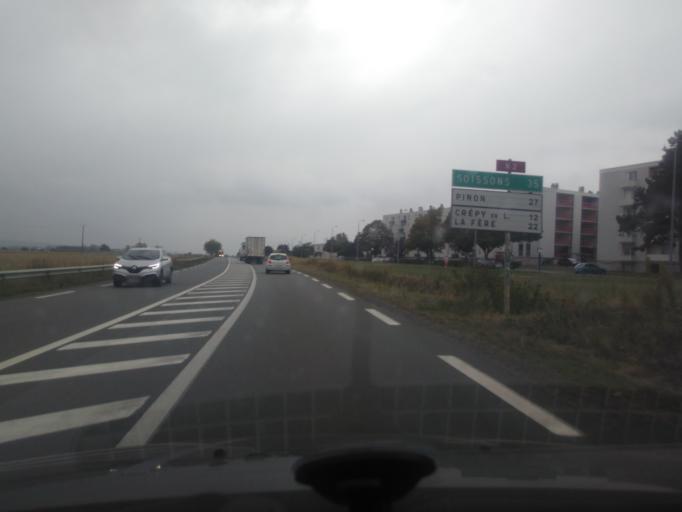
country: FR
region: Picardie
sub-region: Departement de l'Aisne
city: Laon
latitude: 49.5630
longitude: 3.6449
